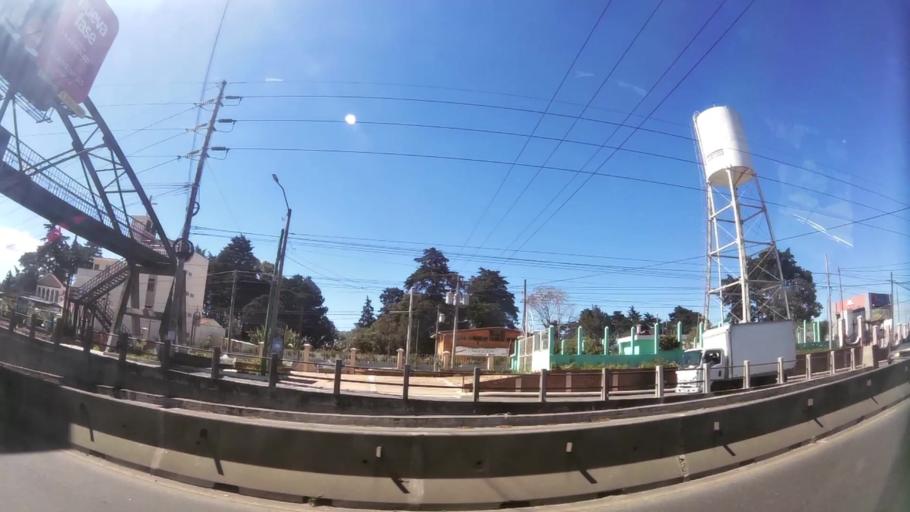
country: GT
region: Guatemala
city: San Jose Pinula
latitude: 14.5440
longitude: -90.4542
